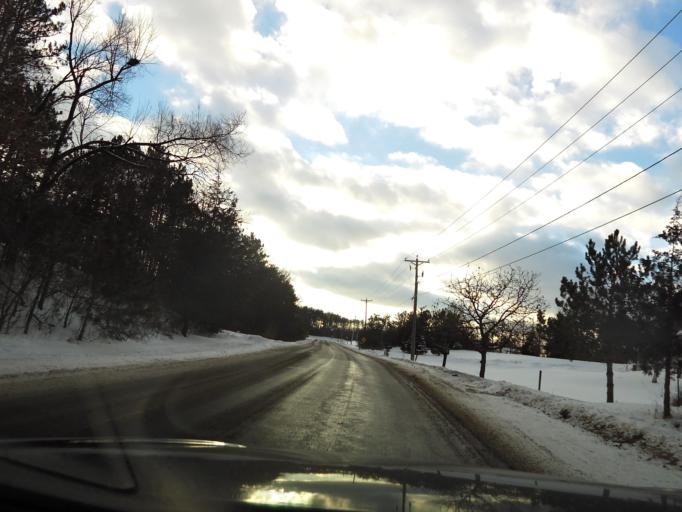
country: US
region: Wisconsin
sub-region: Saint Croix County
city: Hudson
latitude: 44.9793
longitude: -92.7123
